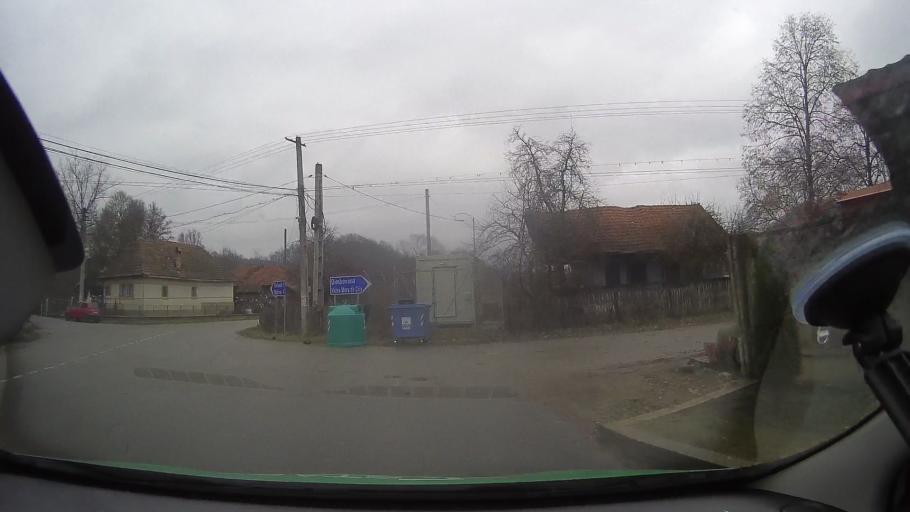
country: RO
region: Hunedoara
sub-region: Comuna Tomesti
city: Tomesti
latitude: 46.2141
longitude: 22.6651
